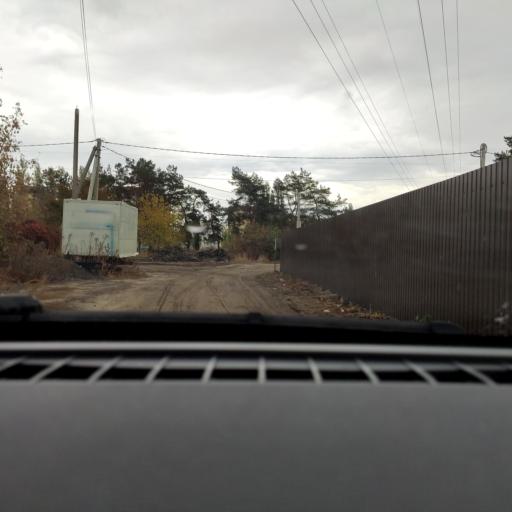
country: RU
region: Voronezj
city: Maslovka
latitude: 51.6026
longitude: 39.2347
